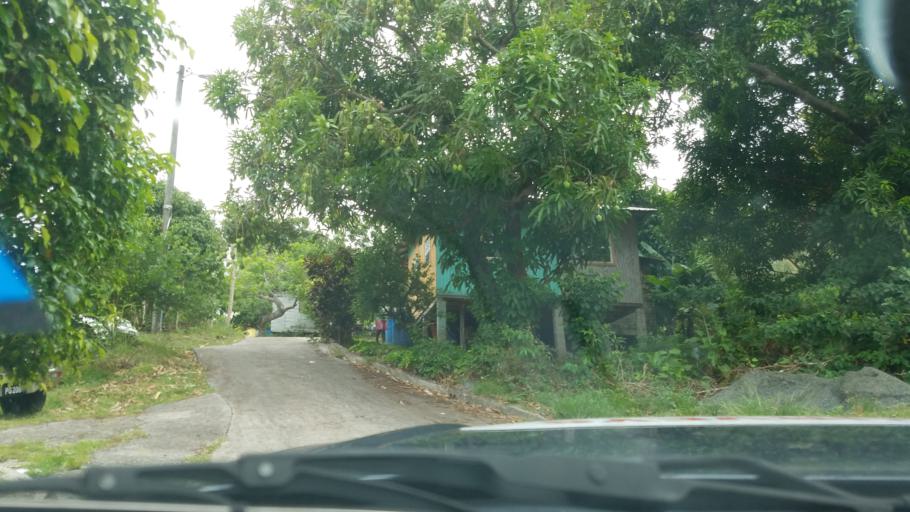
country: LC
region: Castries Quarter
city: Bisee
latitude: 14.0109
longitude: -60.9213
